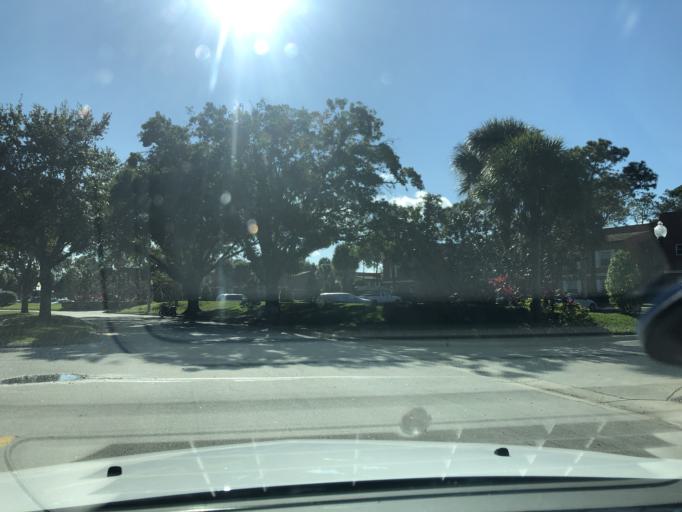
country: US
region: Florida
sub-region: Orange County
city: Oak Ridge
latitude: 28.4910
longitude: -81.4446
